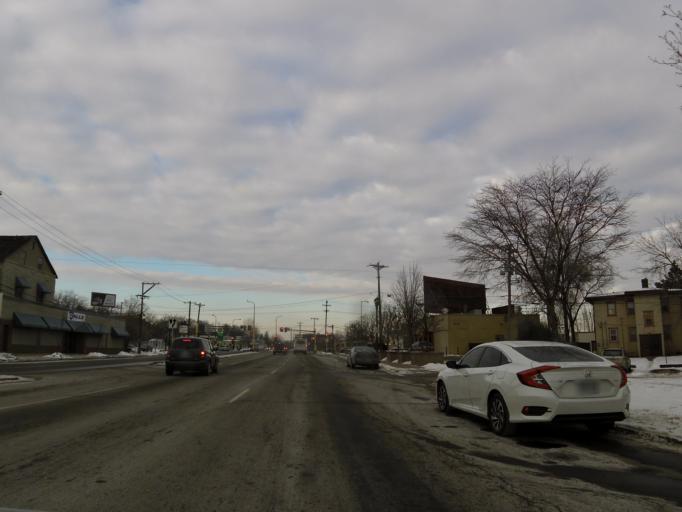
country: US
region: Minnesota
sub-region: Ramsey County
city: Saint Paul
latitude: 44.9690
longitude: -93.1262
